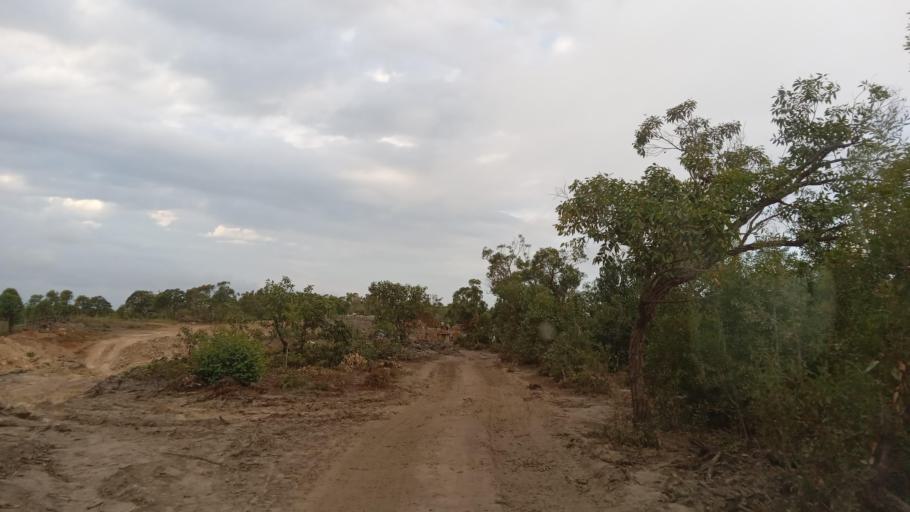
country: MG
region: Atsimo-Atsinanana
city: Vohipaho
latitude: -23.6170
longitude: 47.6032
